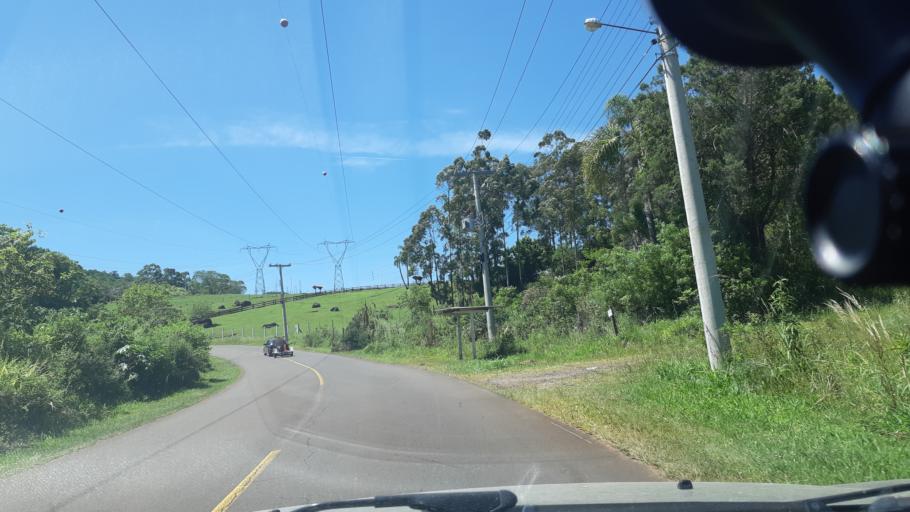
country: BR
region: Rio Grande do Sul
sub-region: Novo Hamburgo
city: Novo Hamburgo
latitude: -29.6262
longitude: -51.1084
